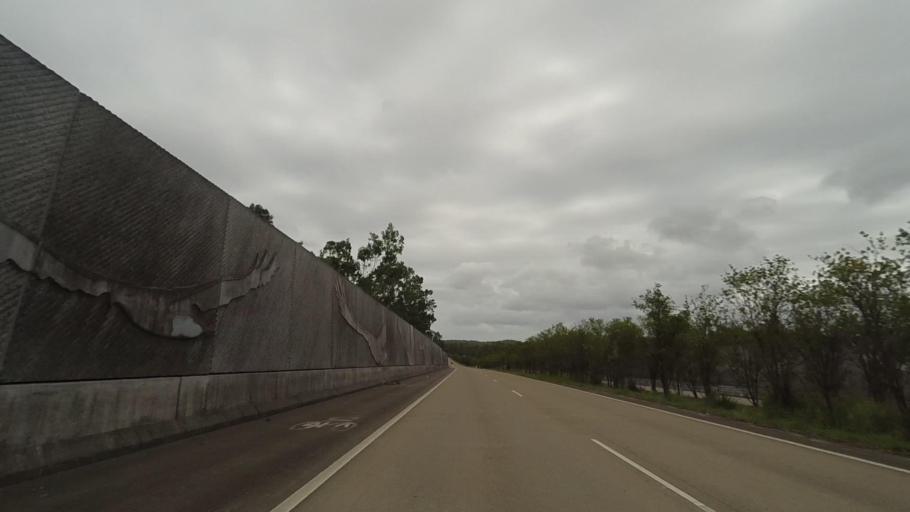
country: AU
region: New South Wales
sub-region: Lake Macquarie Shire
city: Kotara
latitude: -32.9590
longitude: 151.6786
